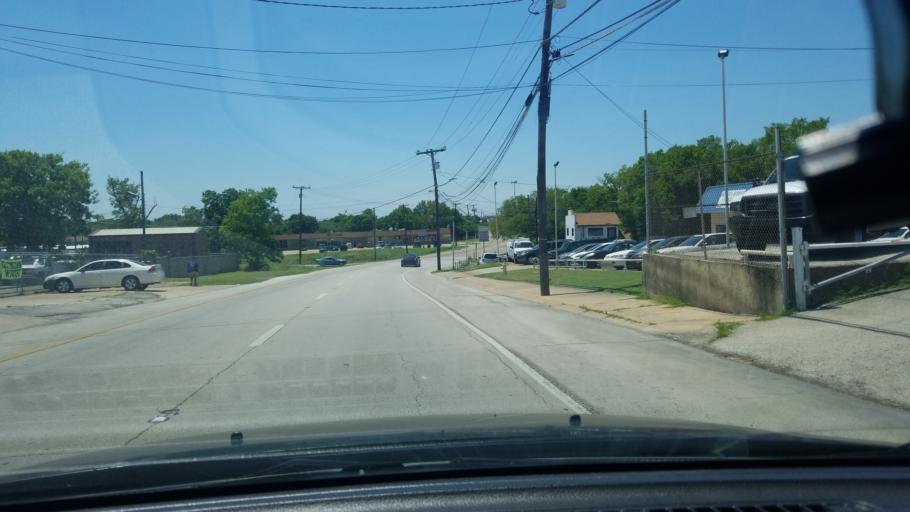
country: US
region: Texas
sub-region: Dallas County
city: Mesquite
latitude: 32.7673
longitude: -96.6044
